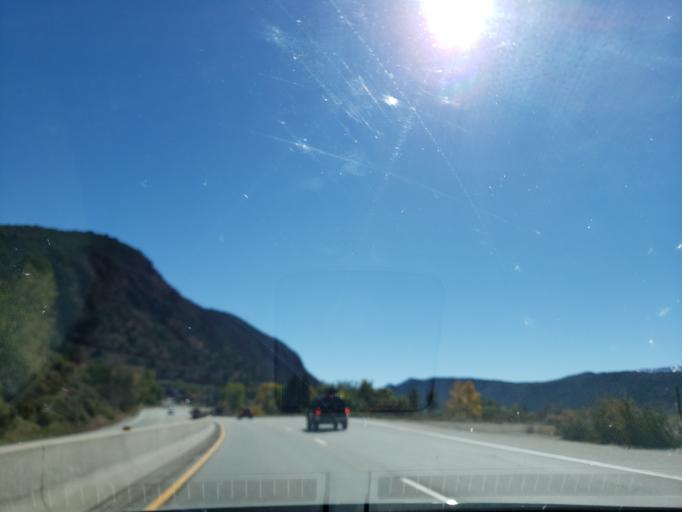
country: US
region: Colorado
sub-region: Garfield County
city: Glenwood Springs
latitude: 39.5070
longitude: -107.3041
